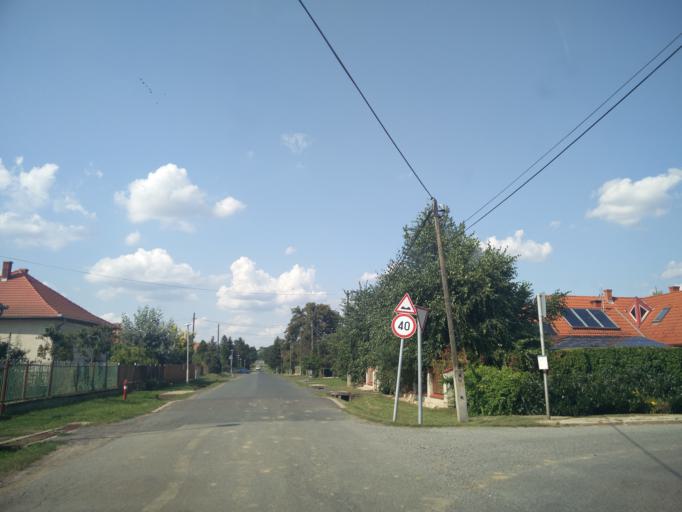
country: HU
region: Zala
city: Zalaegerszeg
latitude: 46.8863
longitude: 16.7933
